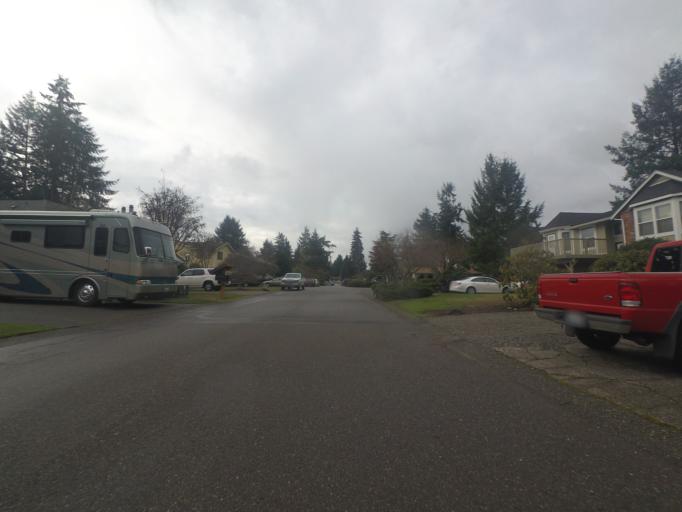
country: US
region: Washington
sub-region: Pierce County
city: University Place
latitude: 47.1986
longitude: -122.5448
